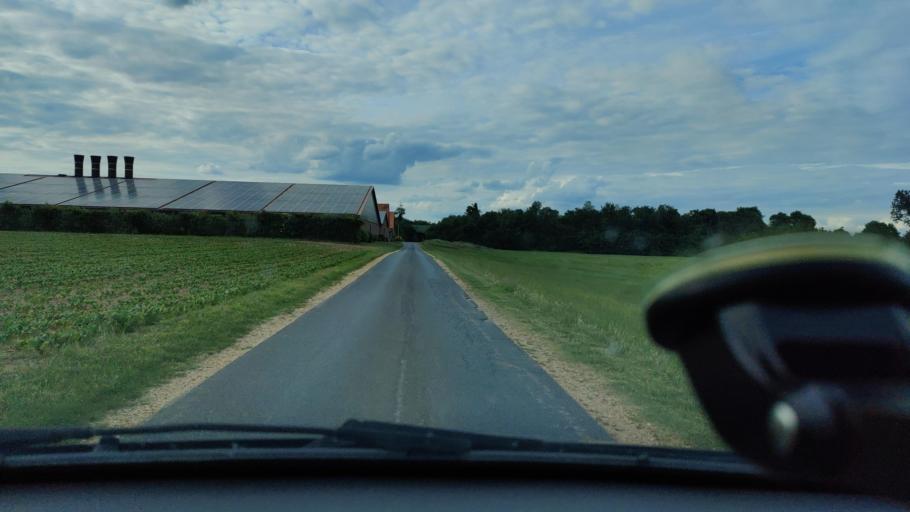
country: DE
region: North Rhine-Westphalia
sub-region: Regierungsbezirk Dusseldorf
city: Weeze
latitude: 51.6513
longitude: 6.1909
